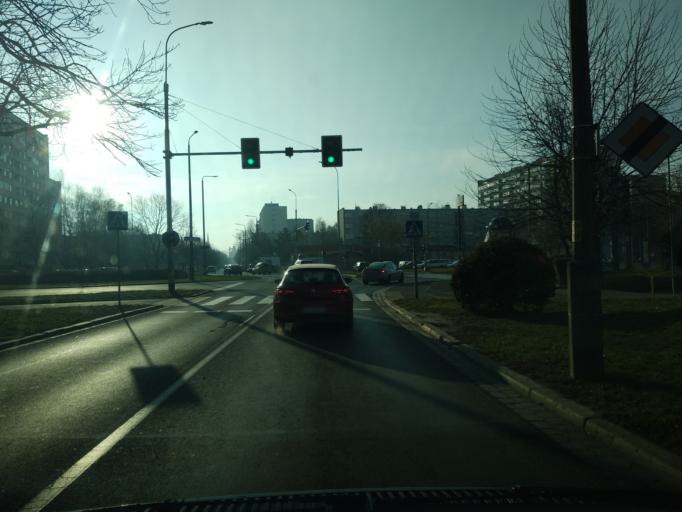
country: PL
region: Lower Silesian Voivodeship
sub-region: Powiat wroclawski
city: Wroclaw
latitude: 51.0976
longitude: 17.0143
